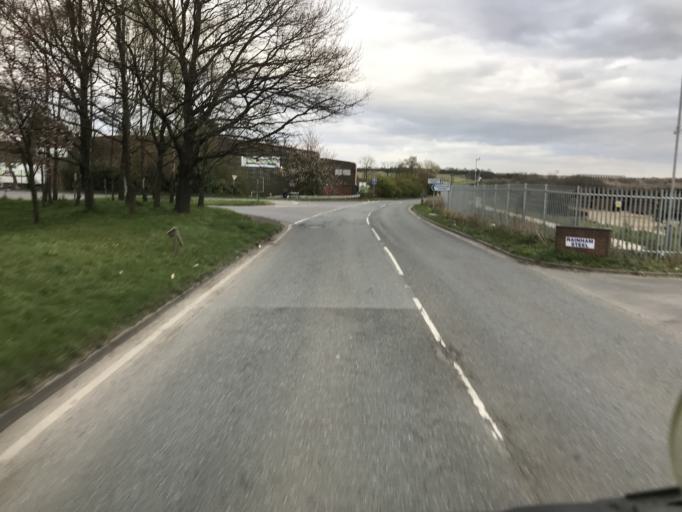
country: GB
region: England
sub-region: North Lincolnshire
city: Burton upon Stather
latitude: 53.6184
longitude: -0.6978
